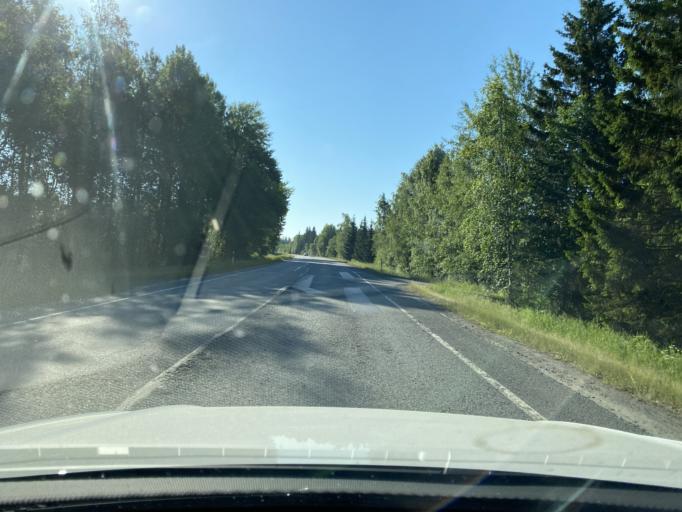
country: FI
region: Haeme
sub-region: Forssa
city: Tammela
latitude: 60.8279
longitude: 23.7362
